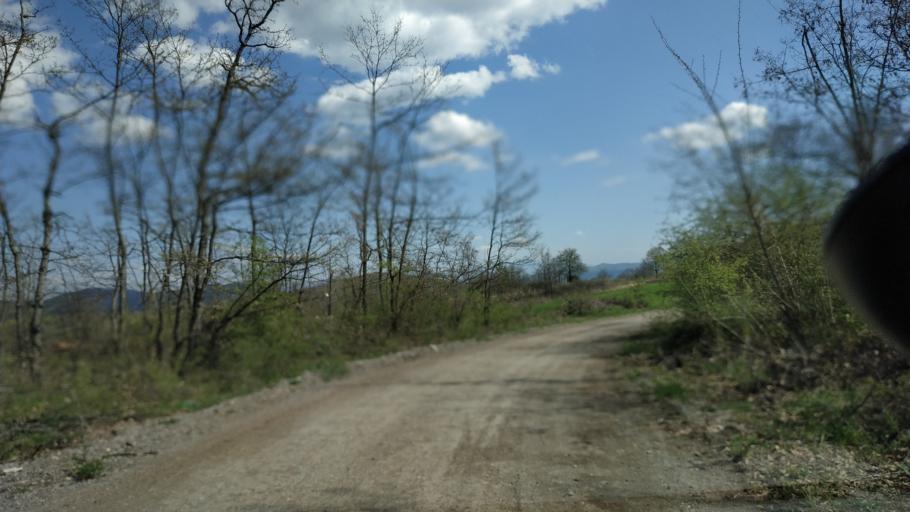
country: RS
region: Central Serbia
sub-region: Zajecarski Okrug
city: Soko Banja
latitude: 43.5473
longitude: 21.9005
